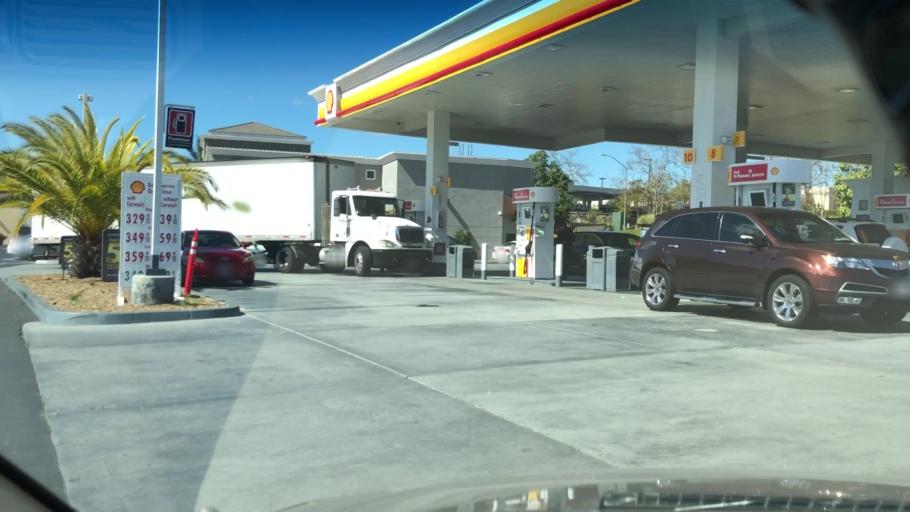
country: US
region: California
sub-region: San Diego County
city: Poway
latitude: 32.9849
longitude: -117.0759
